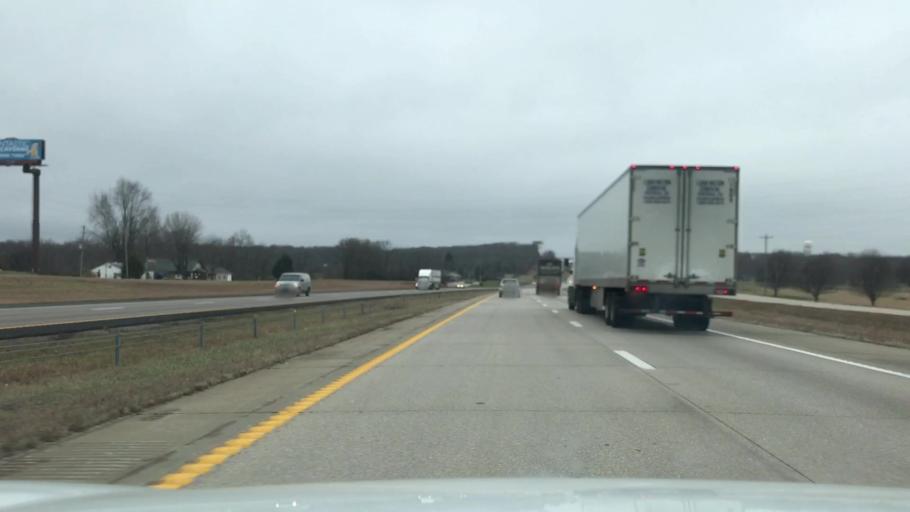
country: US
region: Missouri
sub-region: Franklin County
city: Sullivan
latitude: 38.1922
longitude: -91.1889
